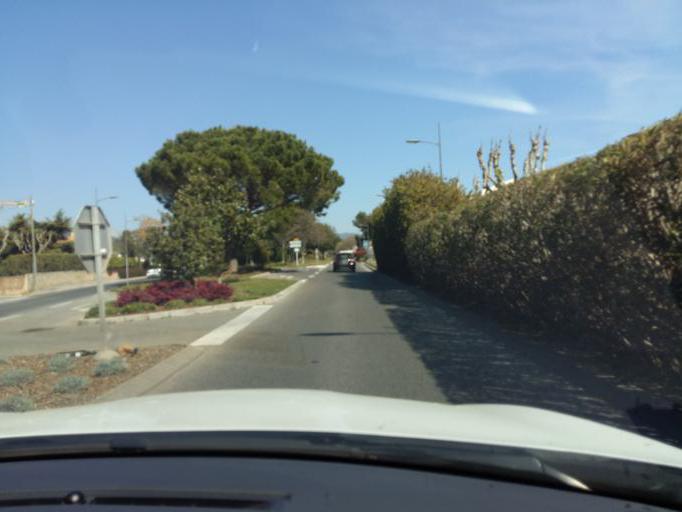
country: FR
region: Provence-Alpes-Cote d'Azur
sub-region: Departement du Var
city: Sanary-sur-Mer
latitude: 43.1210
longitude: 5.8172
